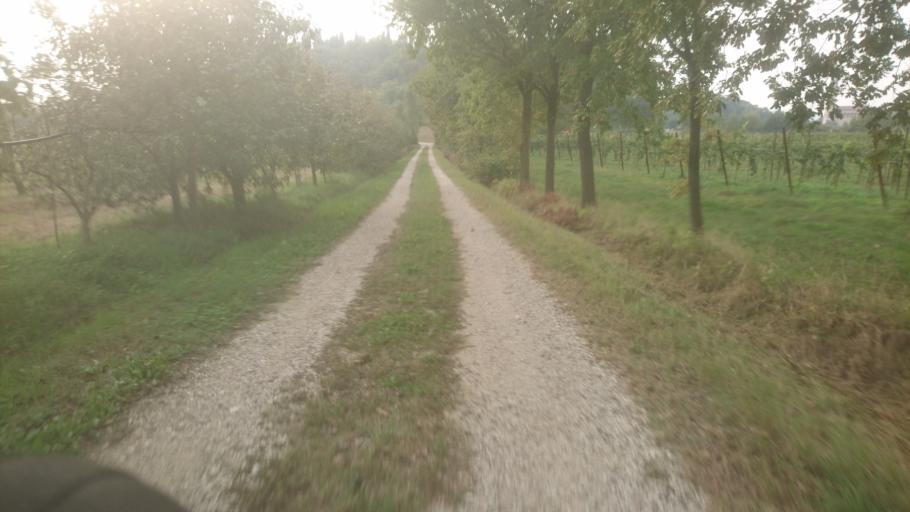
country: IT
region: Veneto
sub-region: Provincia di Vicenza
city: Montegalda
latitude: 45.4447
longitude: 11.6845
